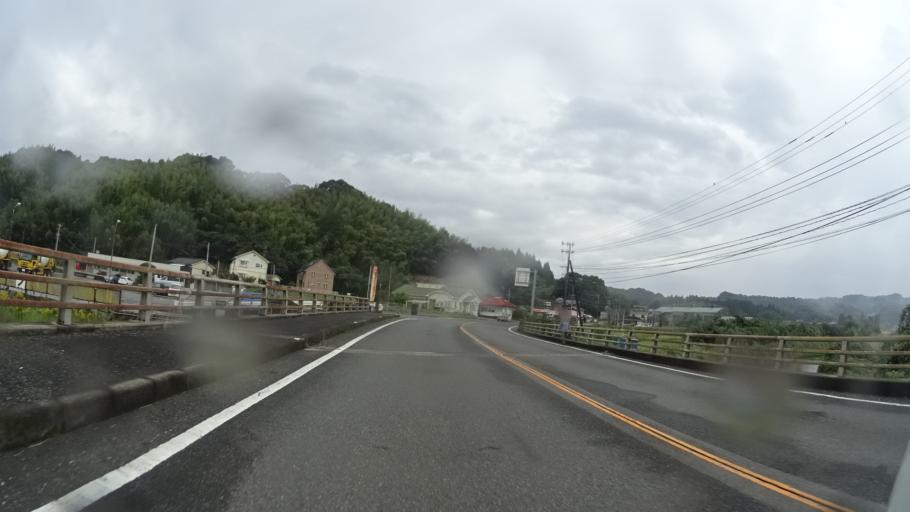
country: JP
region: Kagoshima
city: Kajiki
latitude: 31.7575
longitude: 130.6760
